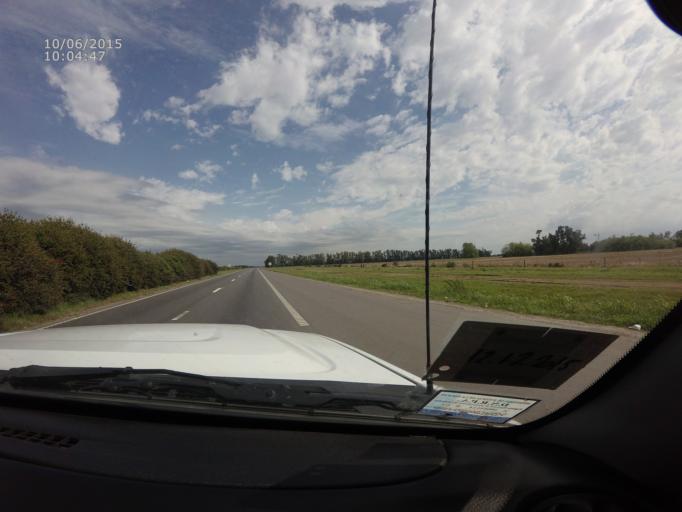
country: AR
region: Buenos Aires
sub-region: Partido de Baradero
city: Baradero
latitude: -33.8494
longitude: -59.5516
